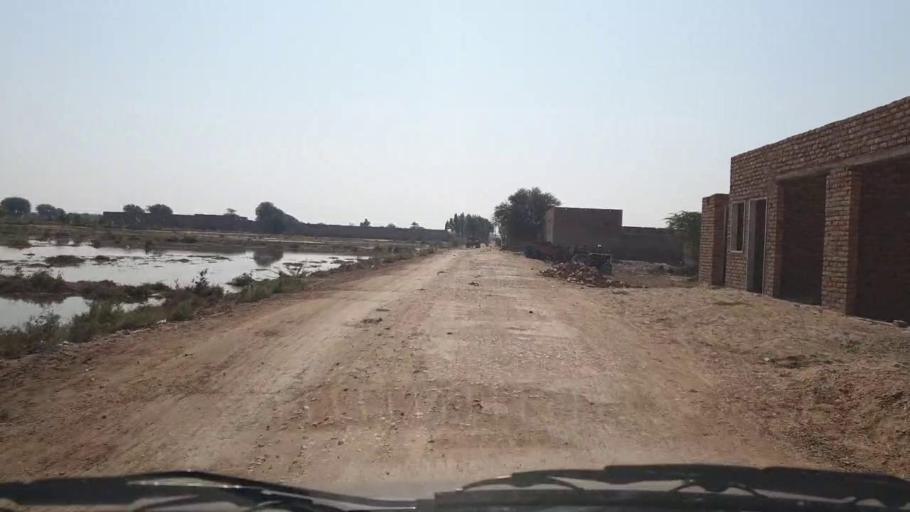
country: PK
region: Sindh
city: Samaro
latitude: 25.2770
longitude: 69.2516
